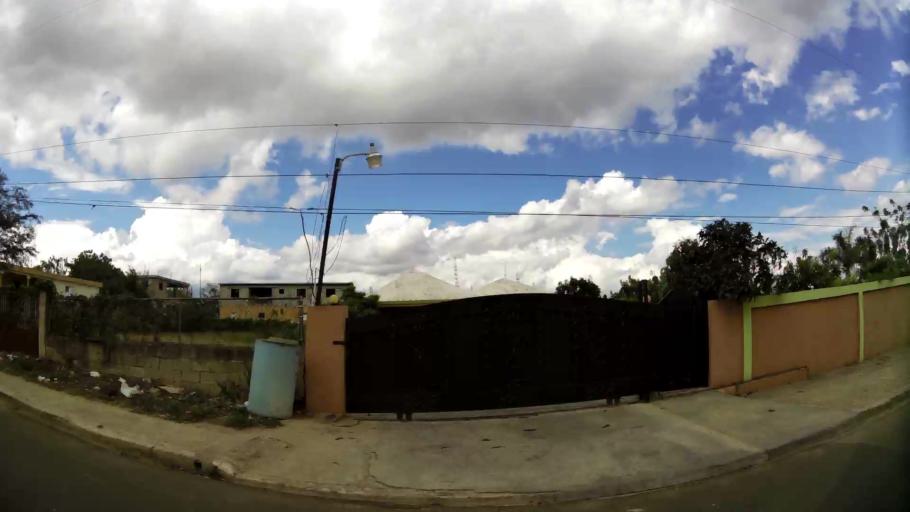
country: DO
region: Santiago
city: Santiago de los Caballeros
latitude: 19.4031
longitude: -70.6577
